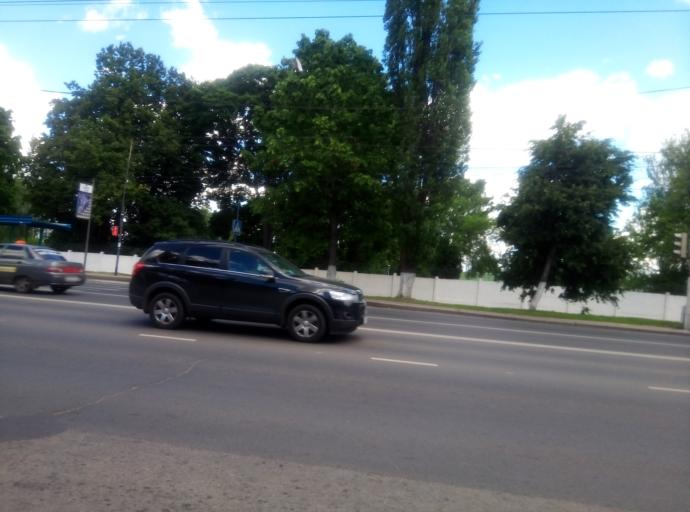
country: RU
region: Kursk
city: Kursk
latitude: 51.7706
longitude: 36.1809
